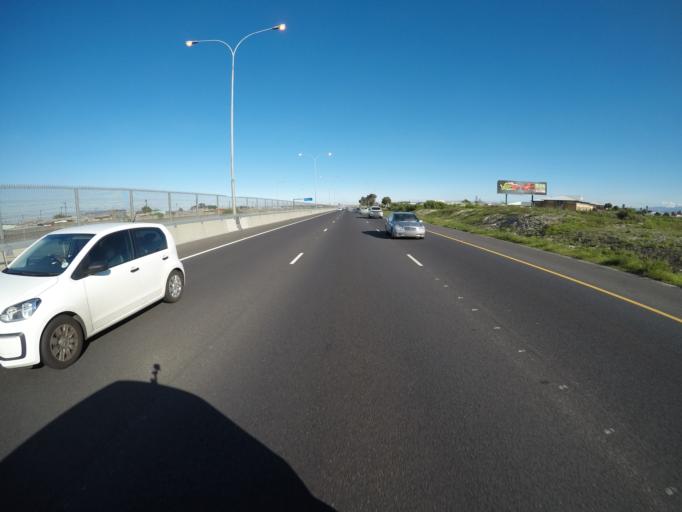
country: ZA
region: Western Cape
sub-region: City of Cape Town
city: Kraaifontein
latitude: -33.9718
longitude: 18.6538
